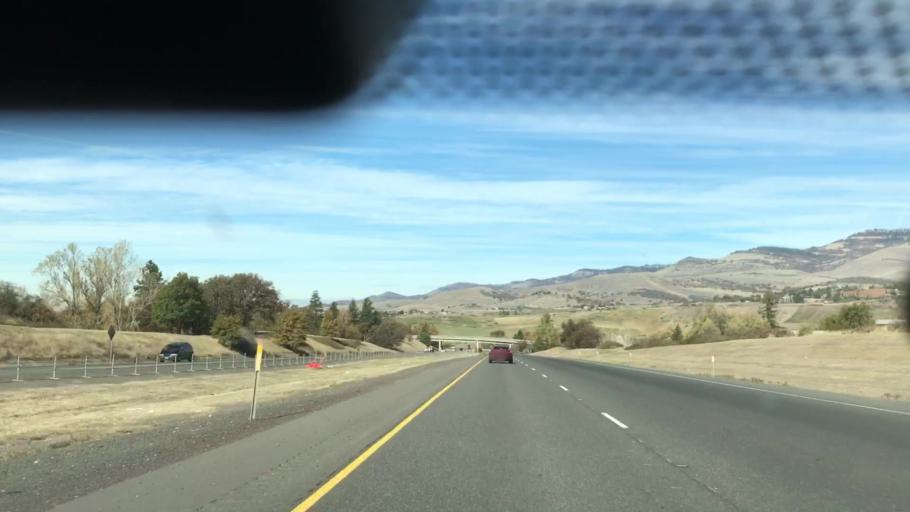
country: US
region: Oregon
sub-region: Jackson County
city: Ashland
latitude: 42.1885
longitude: -122.6682
